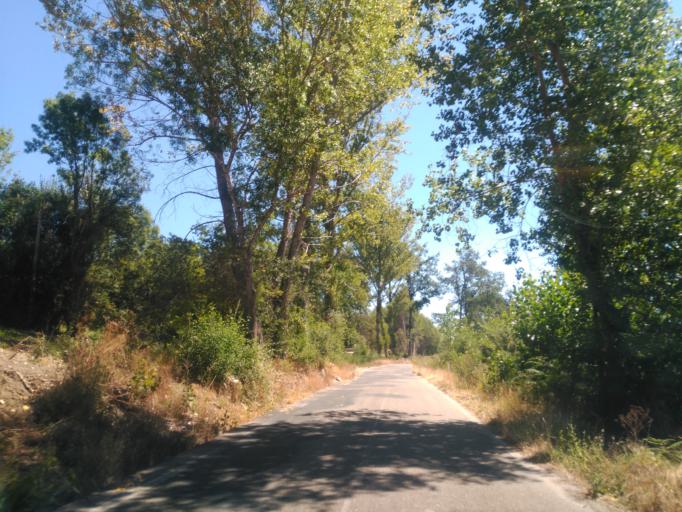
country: ES
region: Castille and Leon
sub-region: Provincia de Zamora
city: Cobreros
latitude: 42.0883
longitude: -6.7069
